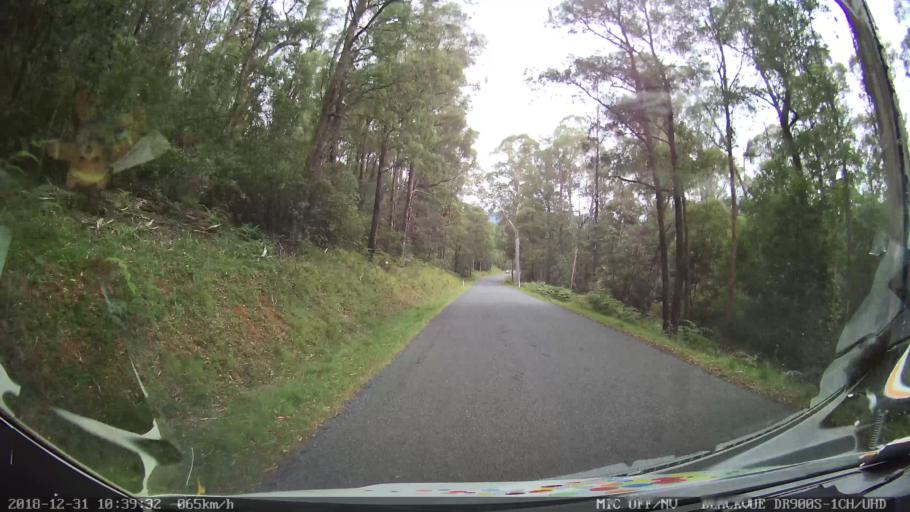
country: AU
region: New South Wales
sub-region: Snowy River
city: Jindabyne
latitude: -36.3982
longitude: 148.1769
